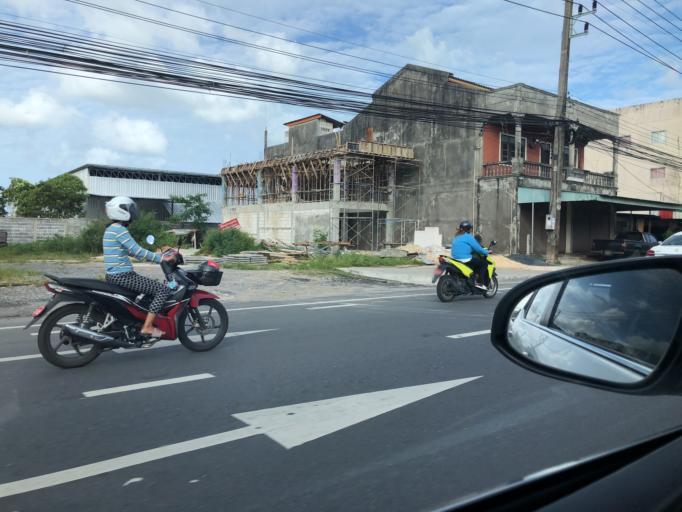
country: TH
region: Phuket
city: Ban Ko Kaeo
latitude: 7.9489
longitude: 98.3914
